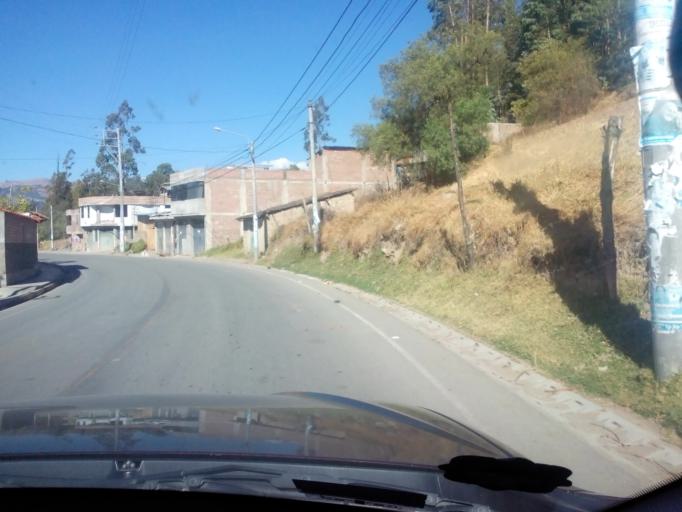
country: PE
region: Apurimac
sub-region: Provincia de Andahuaylas
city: Talavera
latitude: -13.6596
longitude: -73.4324
